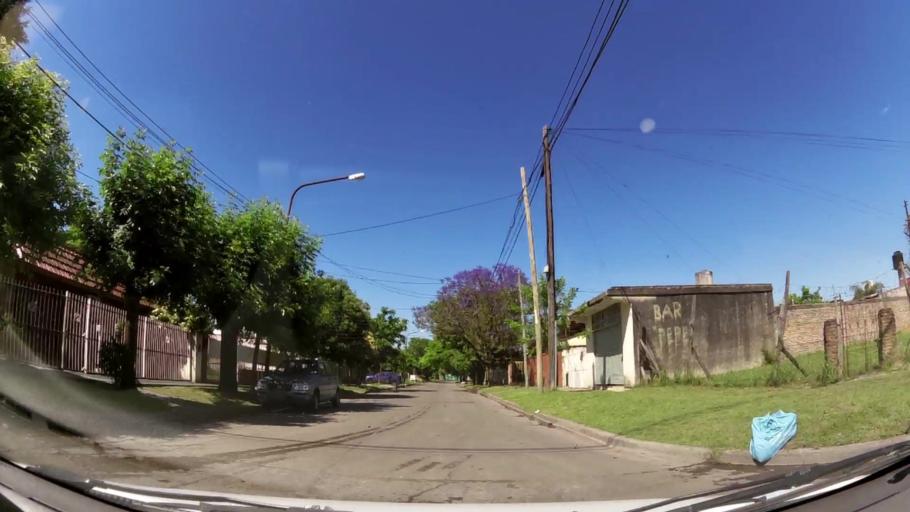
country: AR
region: Buenos Aires
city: Ituzaingo
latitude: -34.6353
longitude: -58.6645
